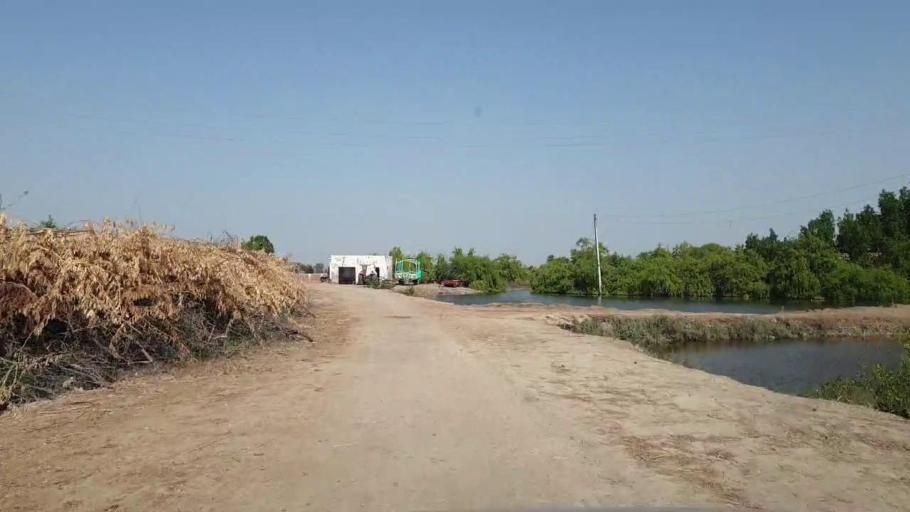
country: PK
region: Sindh
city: Tando Bago
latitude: 24.7549
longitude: 69.0277
